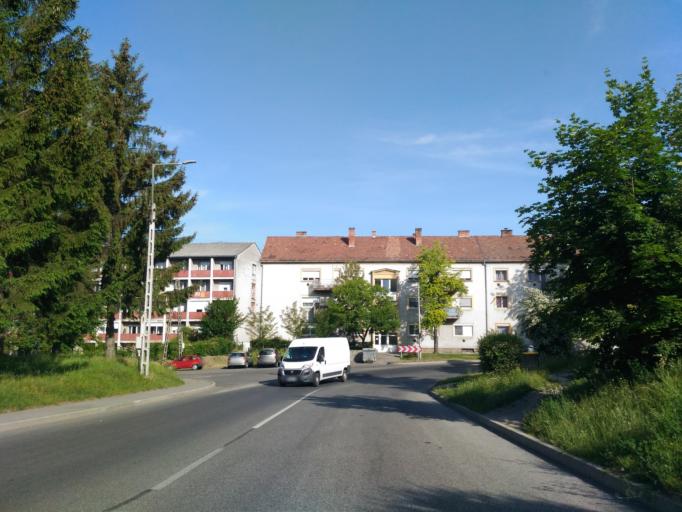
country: HU
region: Baranya
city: Komlo
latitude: 46.1848
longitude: 18.2570
